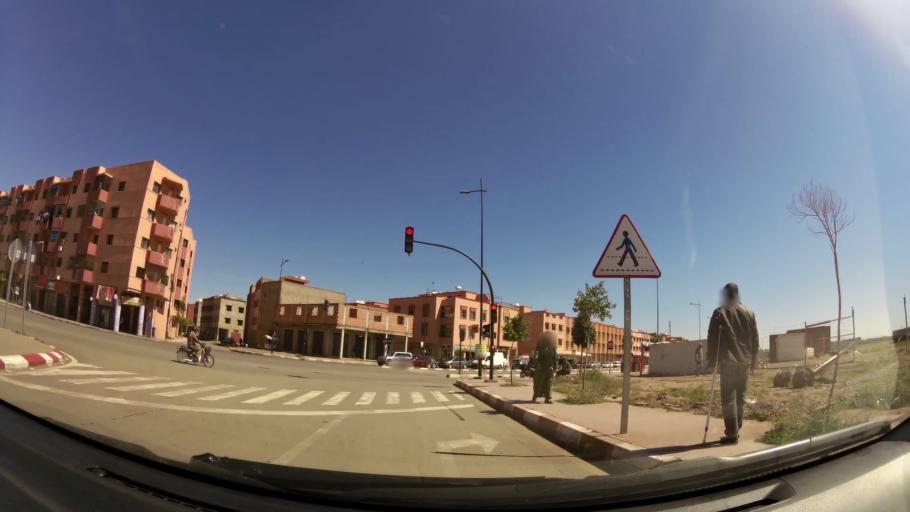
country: MA
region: Marrakech-Tensift-Al Haouz
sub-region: Marrakech
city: Marrakesh
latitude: 31.5810
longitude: -8.0535
